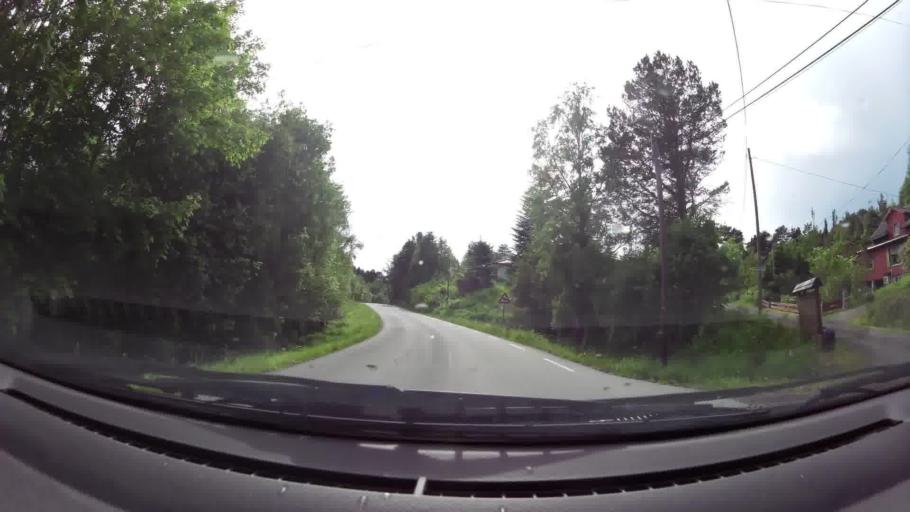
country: NO
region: More og Romsdal
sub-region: Kristiansund
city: Kristiansund
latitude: 63.0304
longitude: 7.7441
